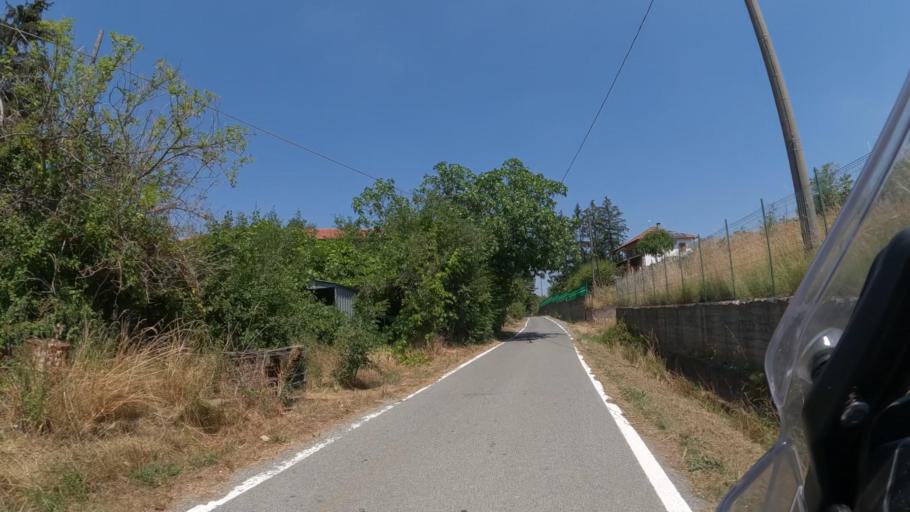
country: IT
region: Piedmont
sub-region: Provincia di Alessandria
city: Ponzone
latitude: 44.5486
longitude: 8.4823
